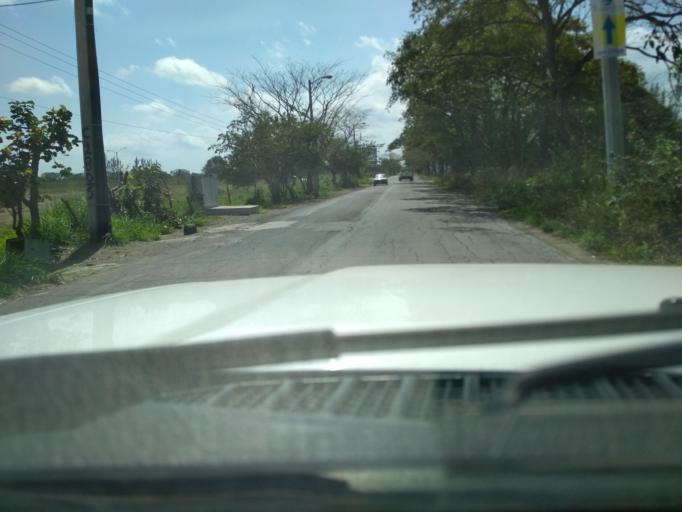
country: MX
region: Veracruz
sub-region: Veracruz
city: Las Amapolas
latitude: 19.1354
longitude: -96.2160
